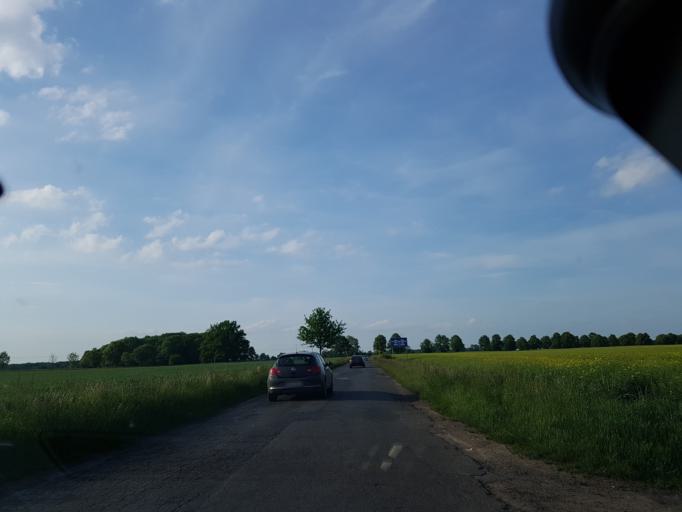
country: PL
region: Lower Silesian Voivodeship
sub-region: Powiat wroclawski
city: Zorawina
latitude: 50.9145
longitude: 17.0029
